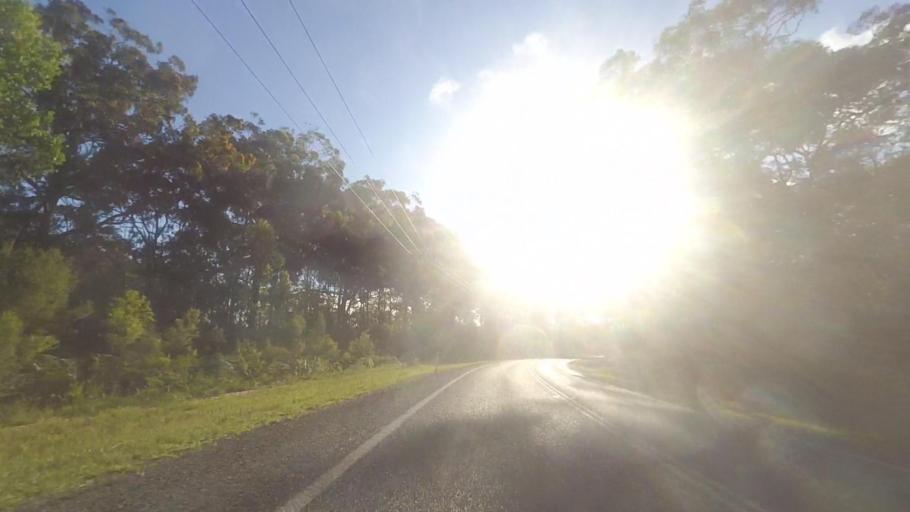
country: AU
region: New South Wales
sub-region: Great Lakes
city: Nabiac
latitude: -32.0905
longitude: 152.4607
